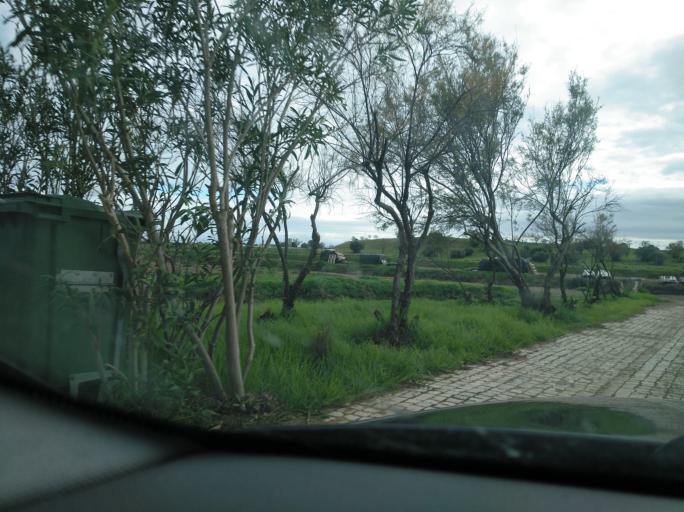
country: PT
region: Faro
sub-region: Castro Marim
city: Castro Marim
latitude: 37.2141
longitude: -7.4407
